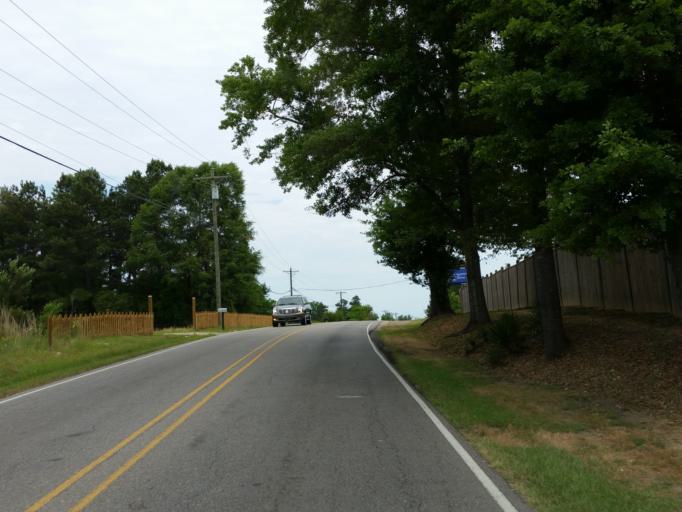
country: US
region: Mississippi
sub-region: Lamar County
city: West Hattiesburg
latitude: 31.3143
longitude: -89.3733
